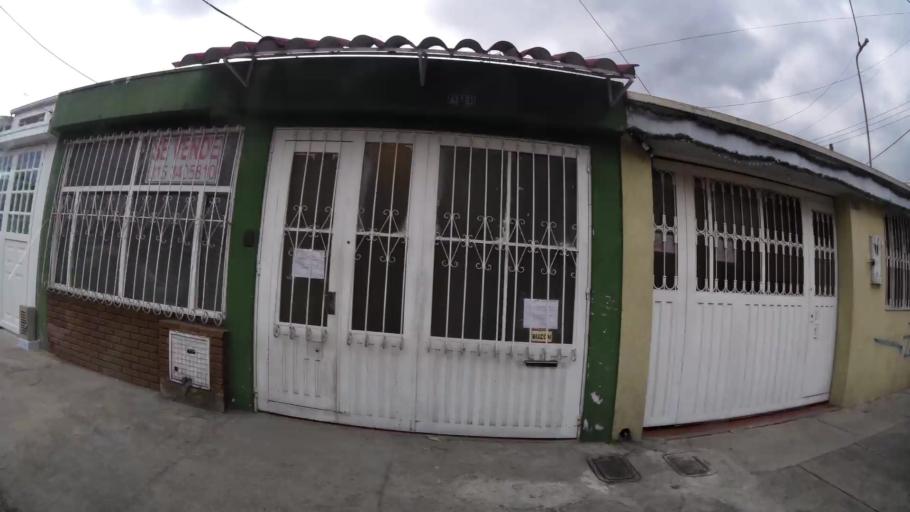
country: CO
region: Bogota D.C.
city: Bogota
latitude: 4.6190
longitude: -74.1159
